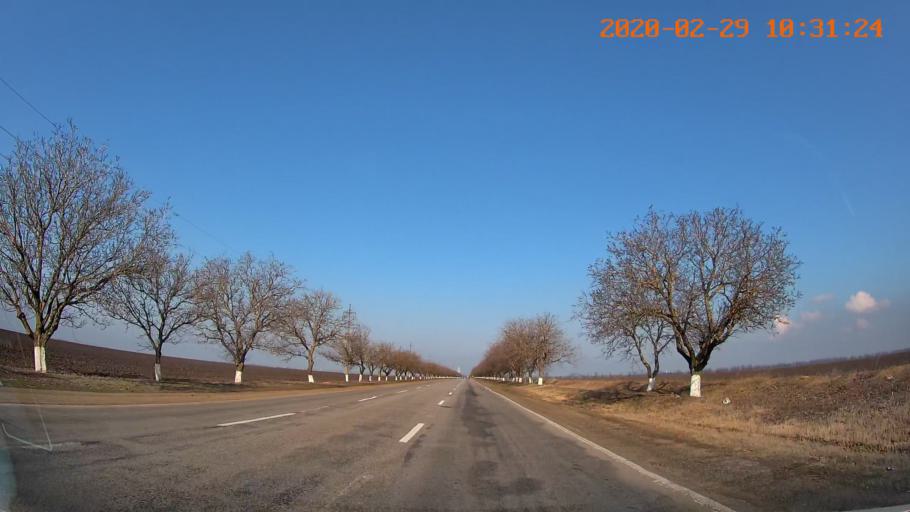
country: MD
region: Telenesti
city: Tiraspolul Nou
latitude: 46.9477
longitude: 29.5646
